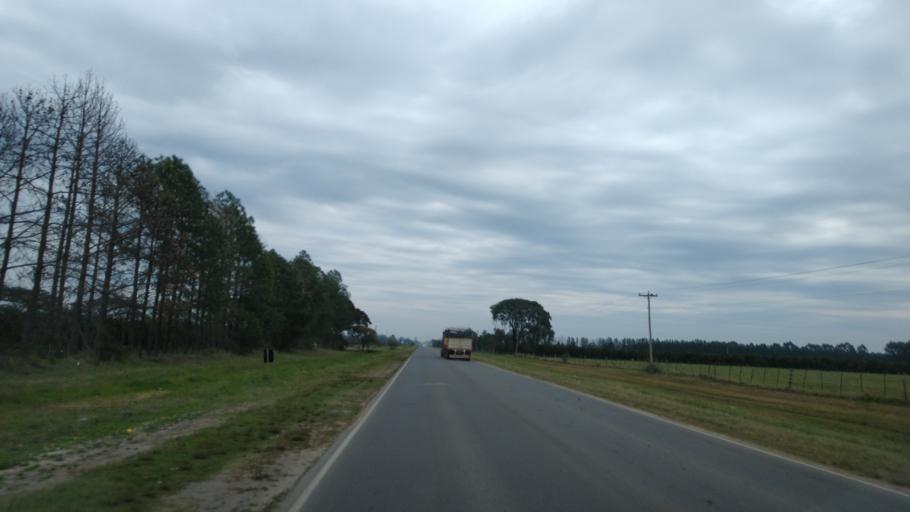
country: AR
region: Entre Rios
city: Villa del Rosario
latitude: -30.7929
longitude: -57.9405
